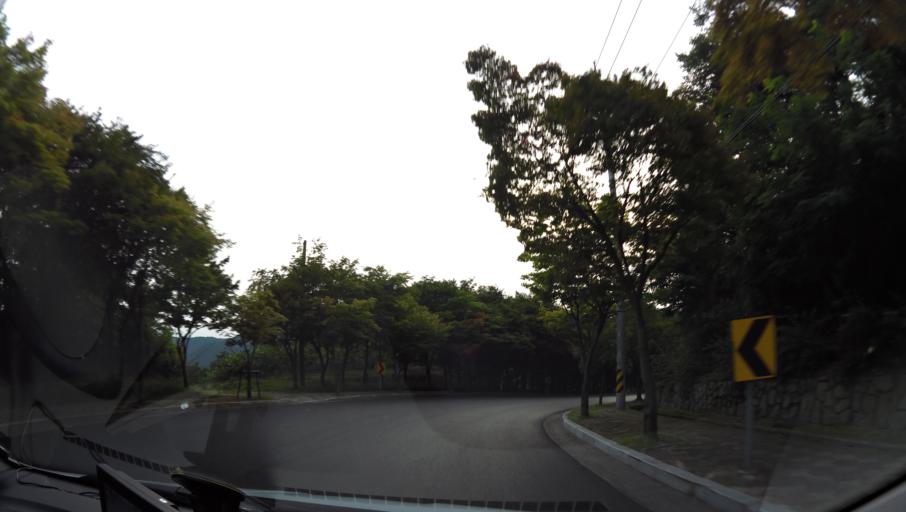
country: KR
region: Daegu
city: Daegu
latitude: 35.9870
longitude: 128.6498
